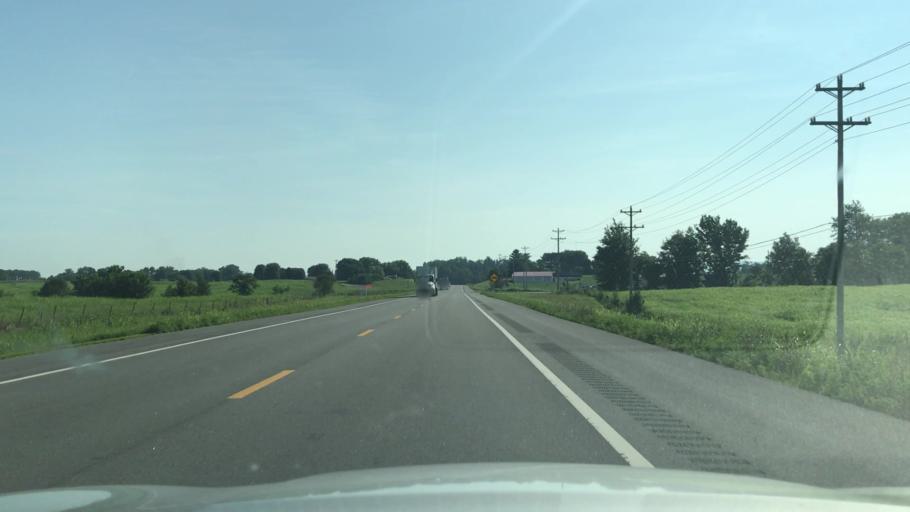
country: US
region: Tennessee
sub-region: Overton County
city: Livingston
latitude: 36.4467
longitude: -85.2174
